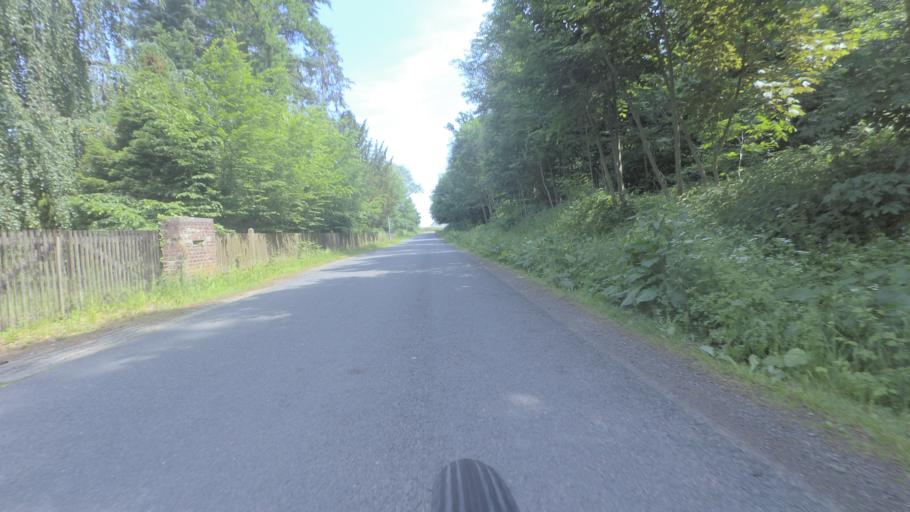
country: DE
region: Saxony-Anhalt
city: Ballenstedt
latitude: 51.7128
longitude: 11.2328
